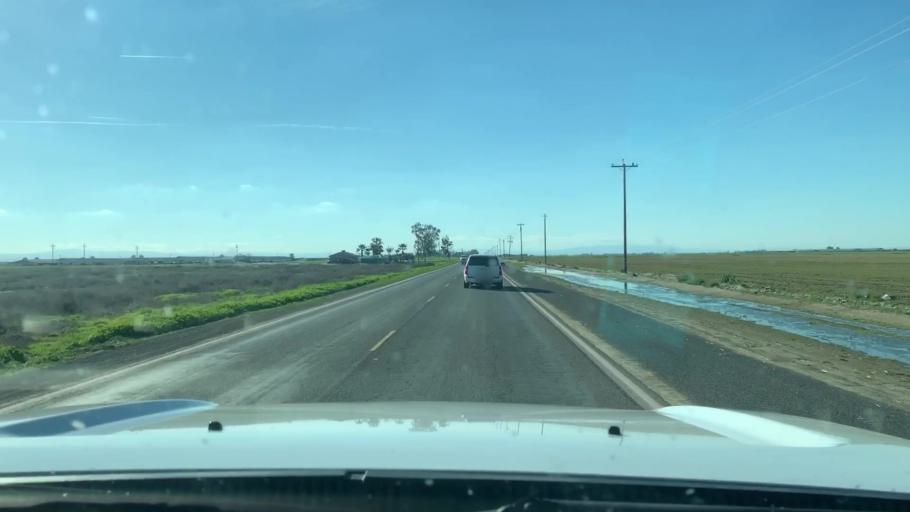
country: US
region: California
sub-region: Kings County
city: Home Garden
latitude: 36.2114
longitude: -119.6771
